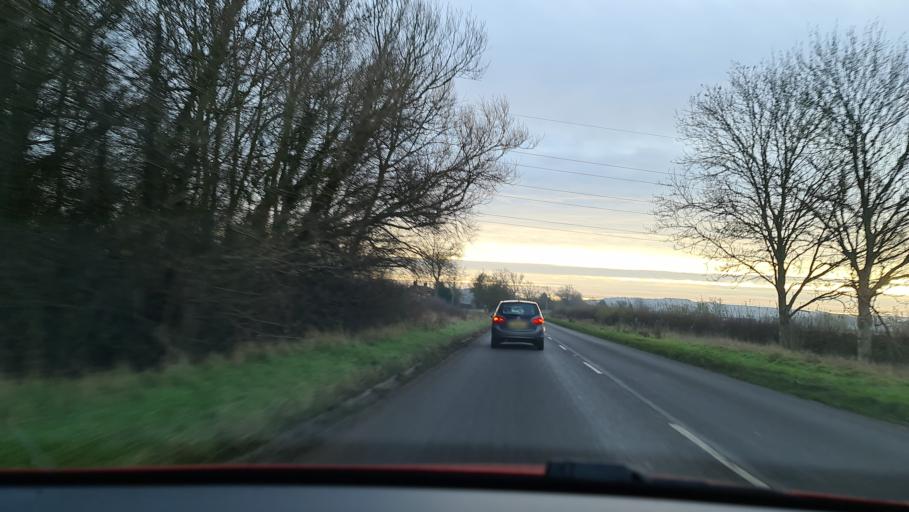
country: GB
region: England
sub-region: Buckinghamshire
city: Haddenham
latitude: 51.7512
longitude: -0.8826
